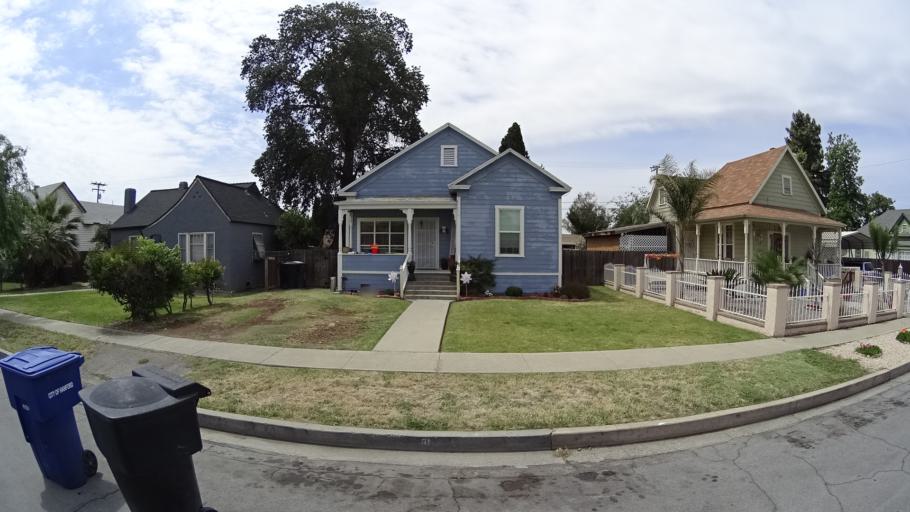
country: US
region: California
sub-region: Kings County
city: Hanford
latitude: 36.3299
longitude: -119.6516
